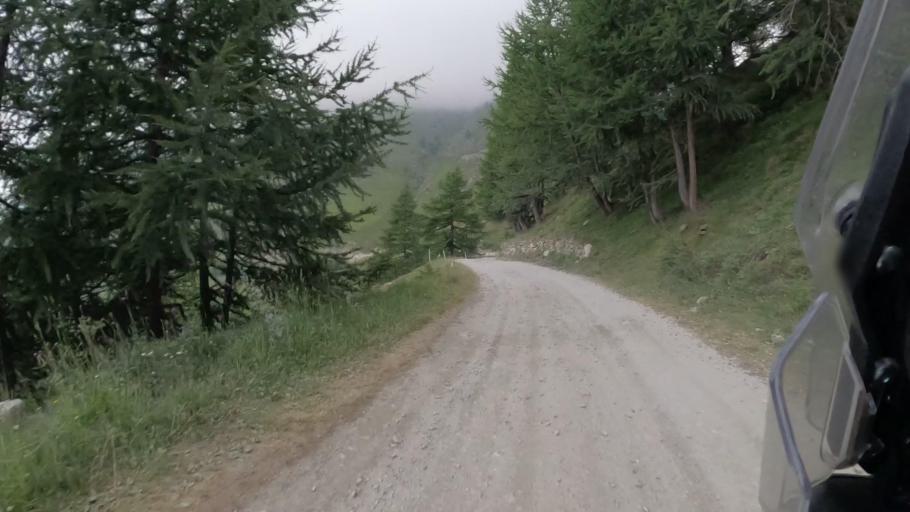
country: IT
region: Piedmont
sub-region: Provincia di Torino
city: Usseaux
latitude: 45.0603
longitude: 6.9997
